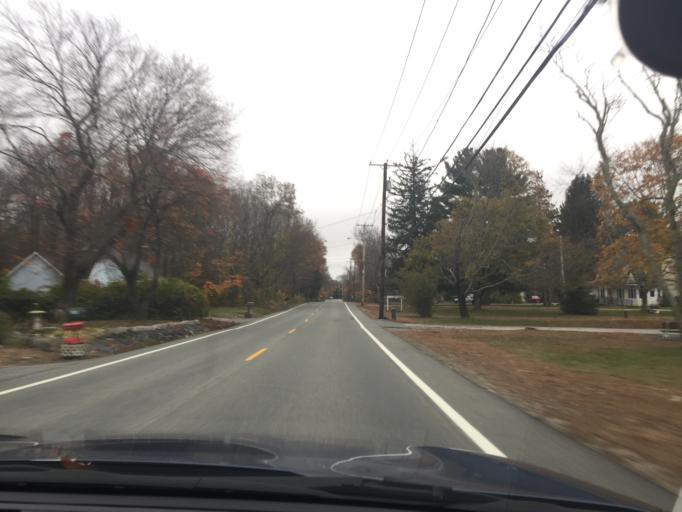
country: US
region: Rhode Island
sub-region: Providence County
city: Chepachet
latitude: 41.8376
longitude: -71.6759
